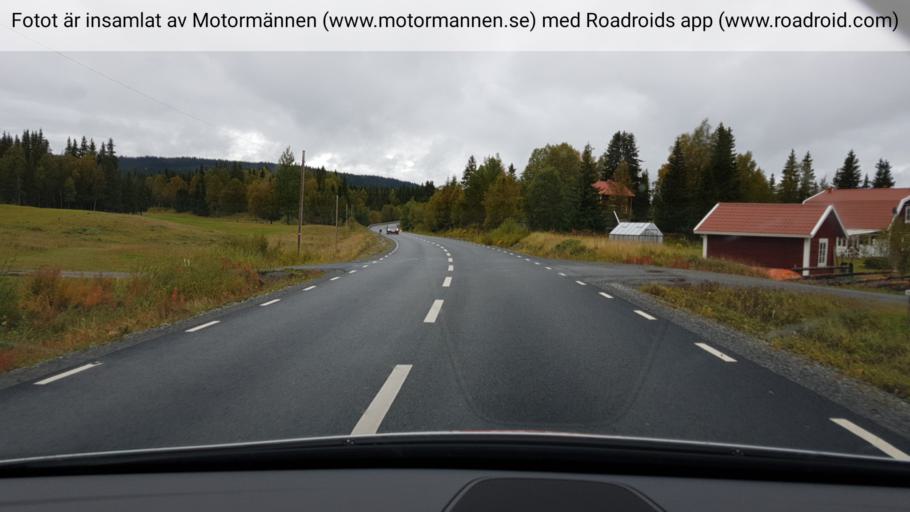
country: SE
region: Jaemtland
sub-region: Are Kommun
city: Are
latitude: 63.4053
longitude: 12.8103
